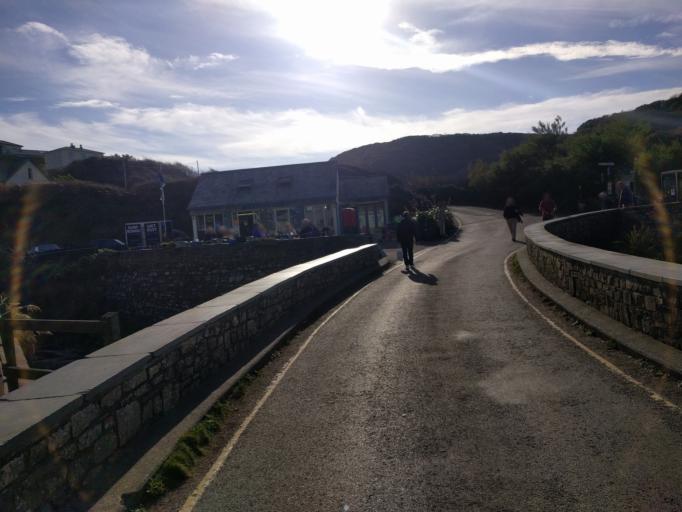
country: GB
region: England
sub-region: Cornwall
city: Jacobstow
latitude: 50.7411
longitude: -4.6331
